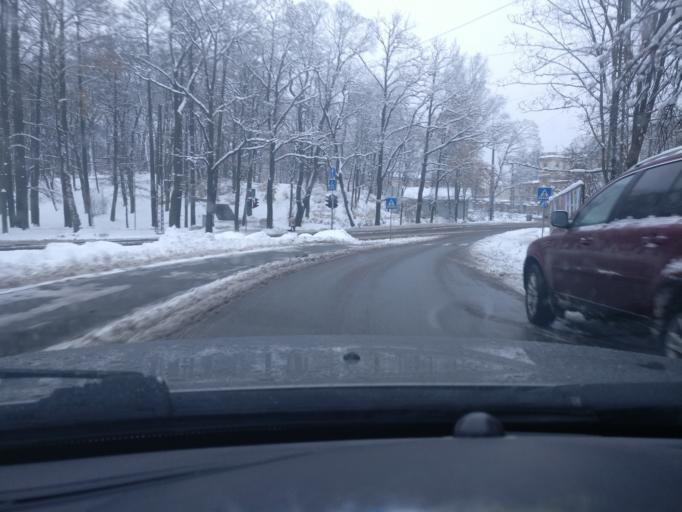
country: LV
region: Riga
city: Riga
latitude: 56.9327
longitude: 24.0824
